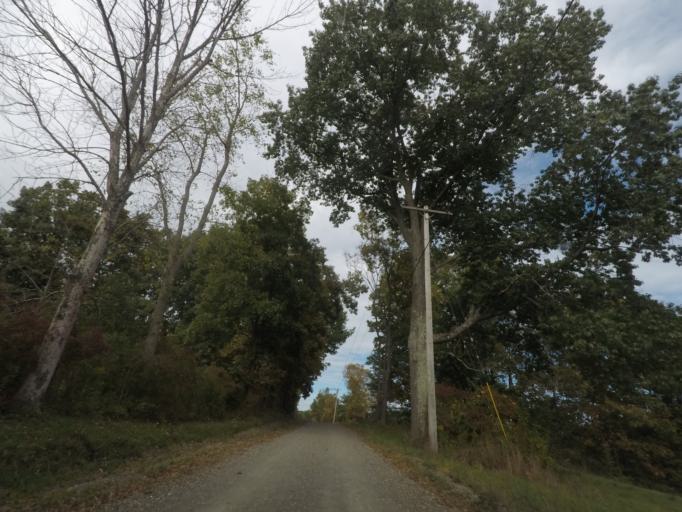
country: US
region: New York
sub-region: Rensselaer County
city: Nassau
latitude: 42.5773
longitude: -73.6141
